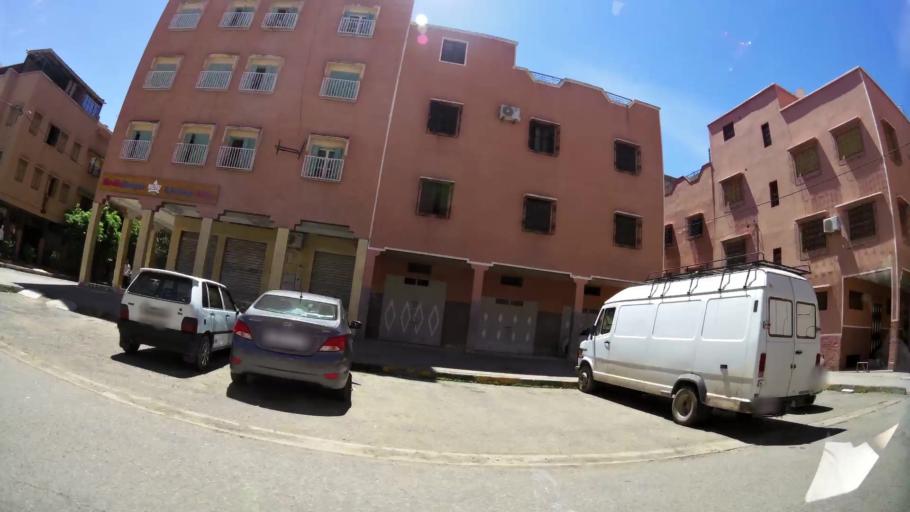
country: MA
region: Marrakech-Tensift-Al Haouz
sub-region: Marrakech
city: Marrakesh
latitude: 31.6302
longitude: -8.0525
